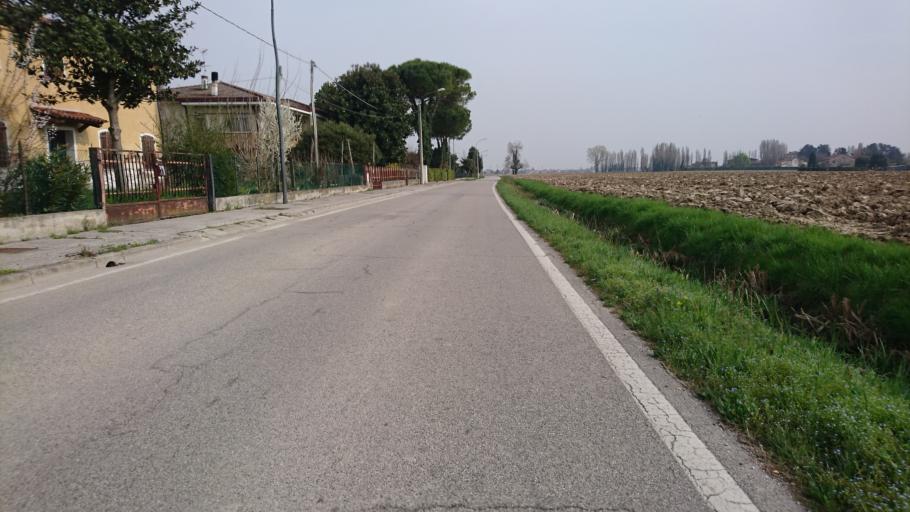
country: IT
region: Veneto
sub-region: Provincia di Padova
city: Selvazzano Dentro
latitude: 45.3785
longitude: 11.7712
